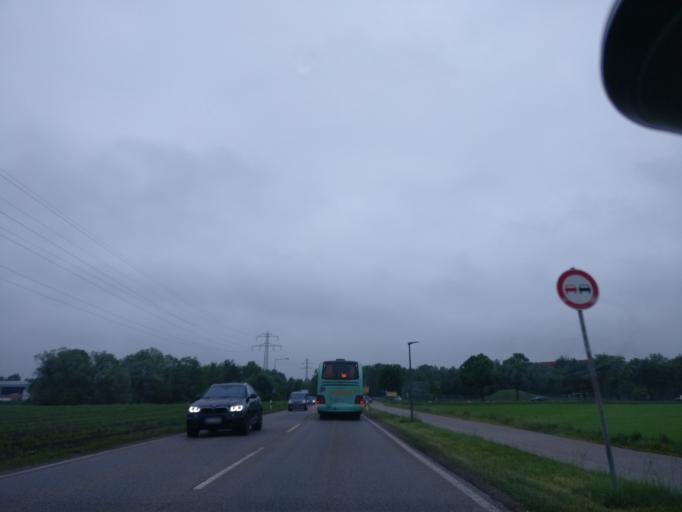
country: DE
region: Bavaria
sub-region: Upper Bavaria
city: Dachau
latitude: 48.2469
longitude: 11.4547
